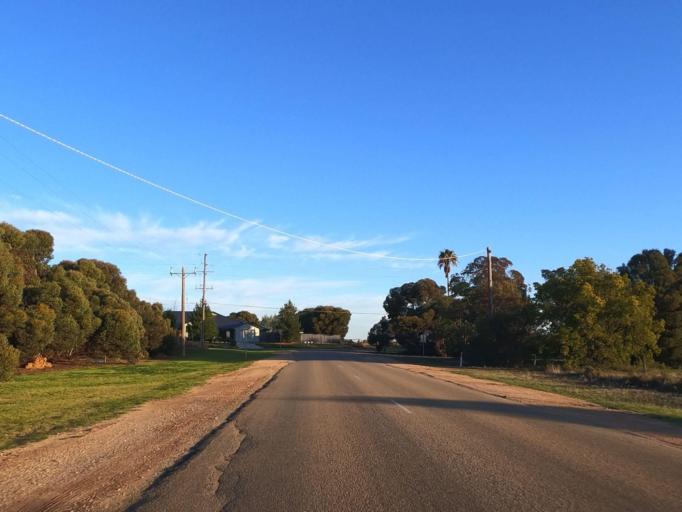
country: AU
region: Victoria
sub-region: Swan Hill
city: Swan Hill
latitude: -35.3597
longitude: 143.5519
